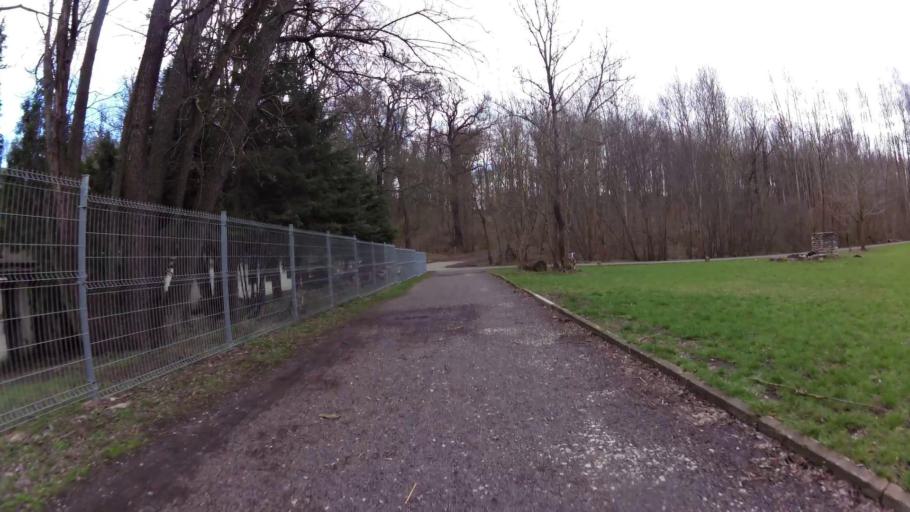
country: DE
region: Thuringia
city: Weimar
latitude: 50.9863
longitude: 11.3351
